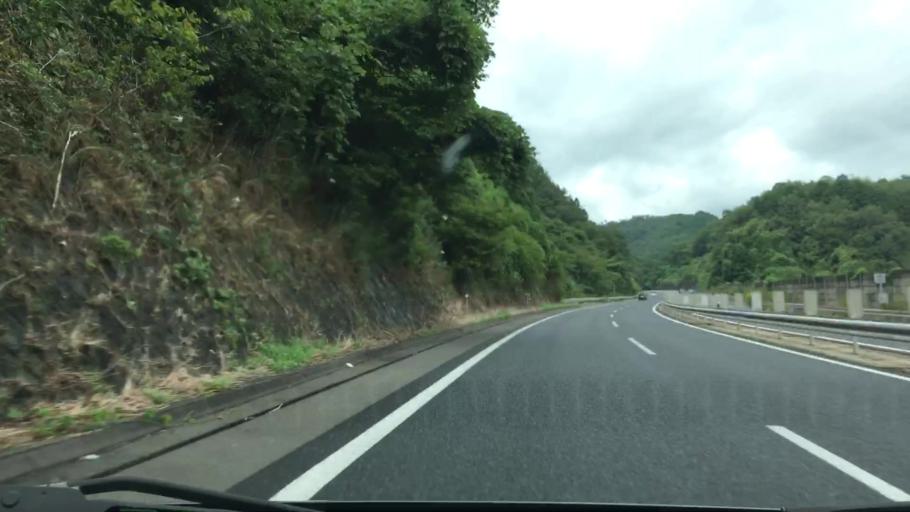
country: JP
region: Hyogo
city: Yamazakicho-nakabirose
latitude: 35.0117
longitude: 134.2865
